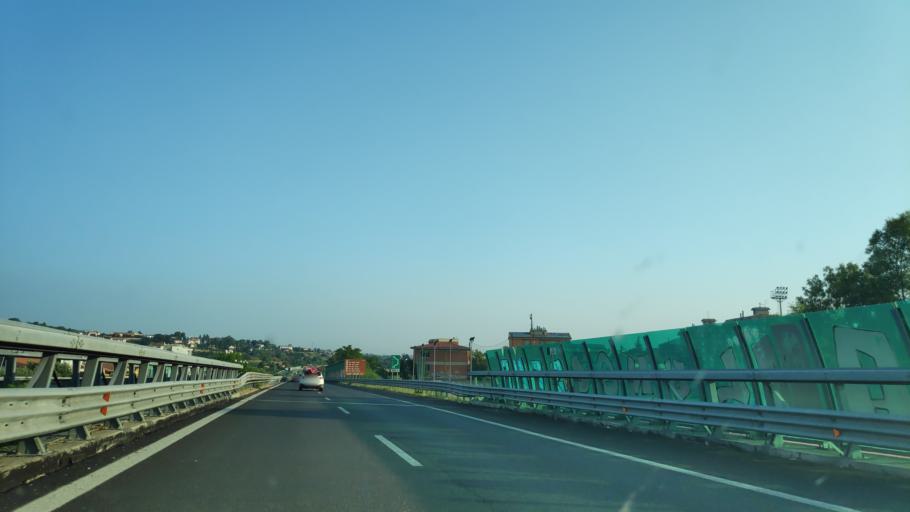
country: IT
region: Calabria
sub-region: Provincia di Cosenza
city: Quattromiglia
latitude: 39.3328
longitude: 16.2376
